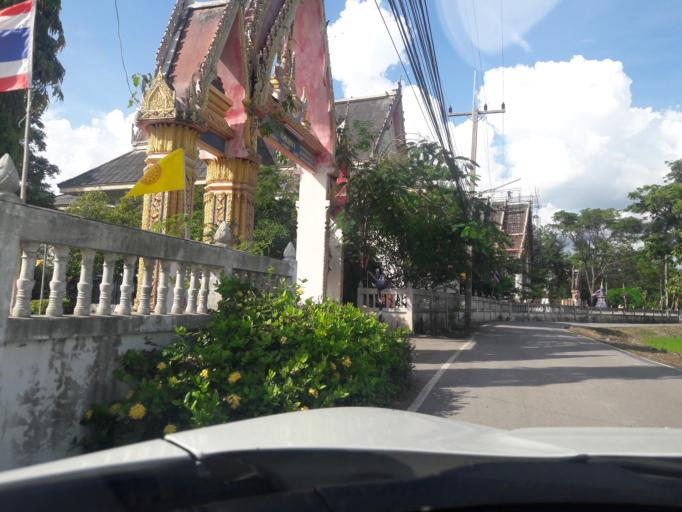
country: TH
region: Lop Buri
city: Ban Mi
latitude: 15.0535
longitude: 100.5378
